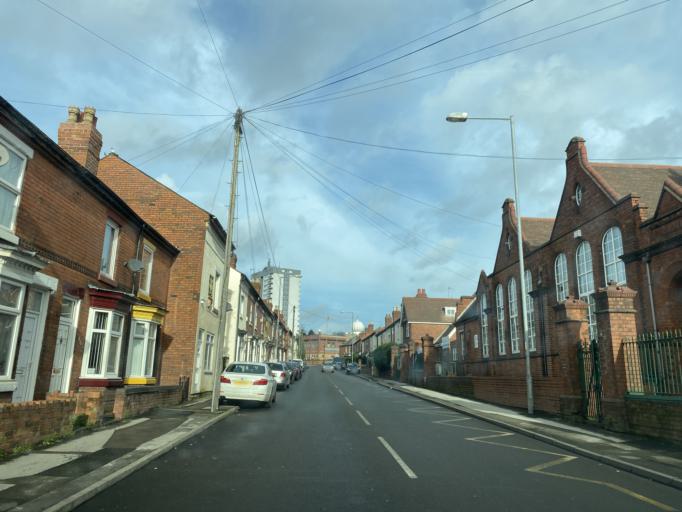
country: GB
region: England
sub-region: Walsall
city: Walsall
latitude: 52.5722
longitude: -1.9800
